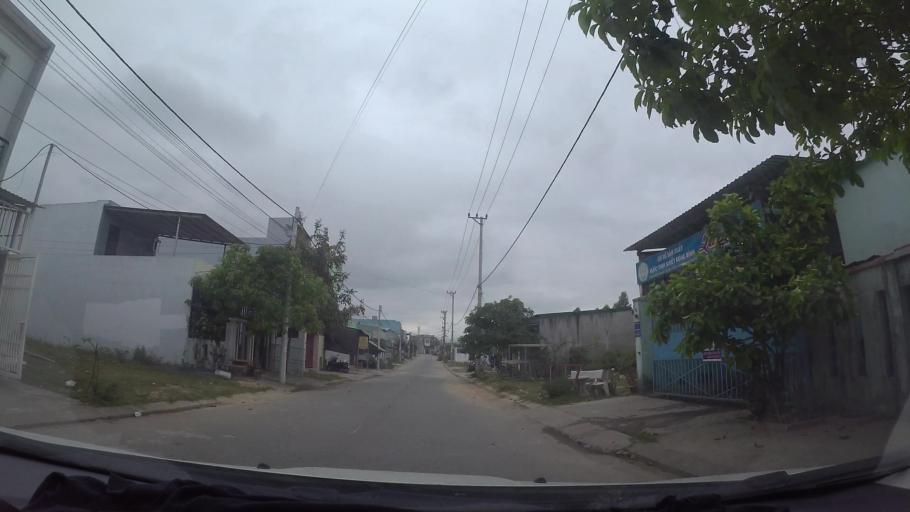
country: VN
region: Da Nang
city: Lien Chieu
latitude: 16.0693
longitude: 108.1408
